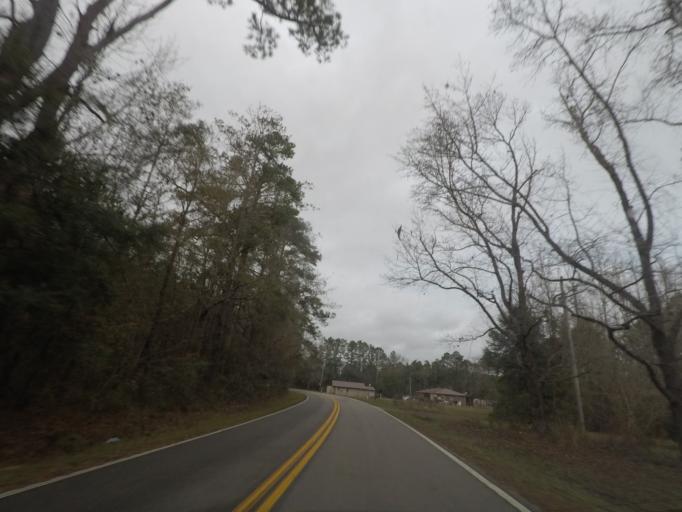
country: US
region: South Carolina
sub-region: Colleton County
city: Walterboro
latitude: 32.9024
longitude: -80.5142
